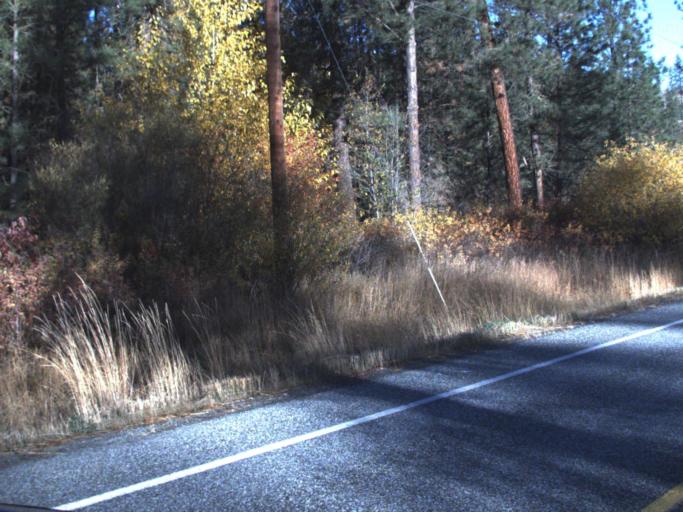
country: US
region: Washington
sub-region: Okanogan County
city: Coulee Dam
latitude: 48.1052
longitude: -118.7000
